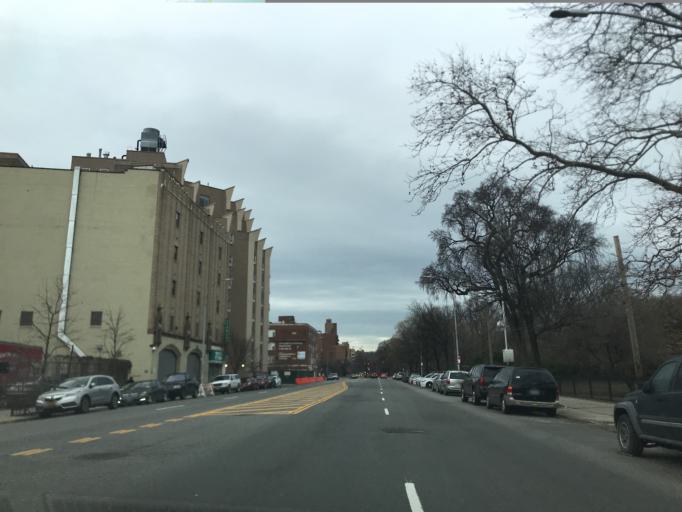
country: US
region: New York
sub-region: Kings County
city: Brooklyn
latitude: 40.6487
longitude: -73.9714
